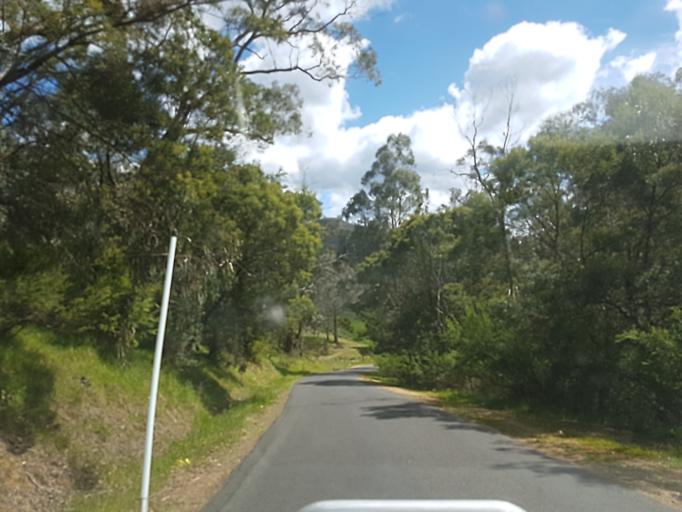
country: AU
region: Victoria
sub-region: East Gippsland
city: Bairnsdale
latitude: -37.4327
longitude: 147.2494
